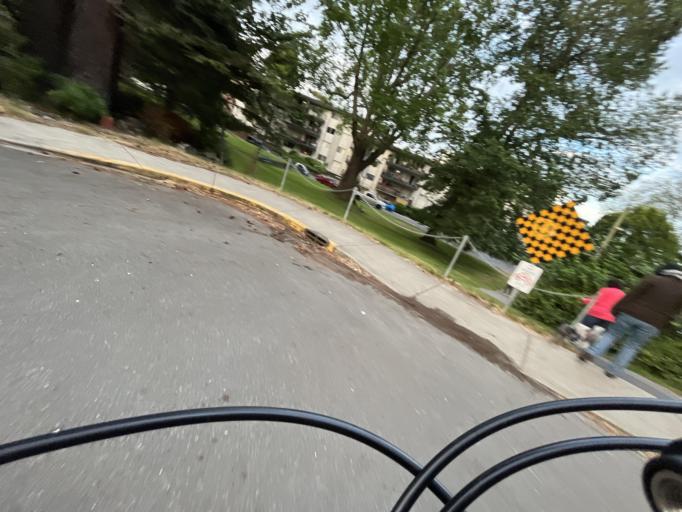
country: CA
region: British Columbia
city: Victoria
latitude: 48.4307
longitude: -123.3937
